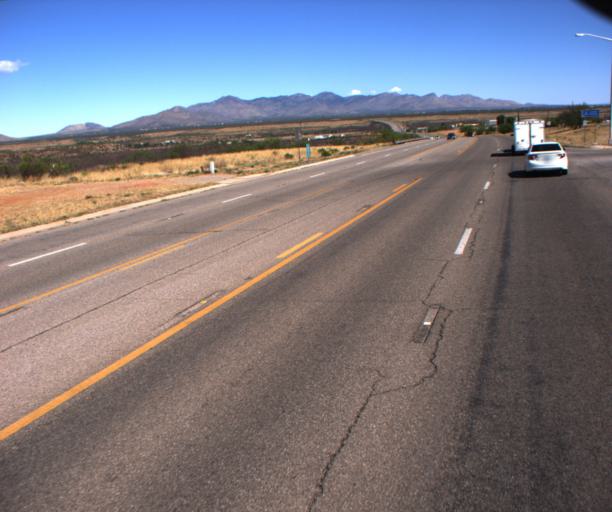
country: US
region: Arizona
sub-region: Cochise County
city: Huachuca City
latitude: 31.6308
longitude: -110.3355
